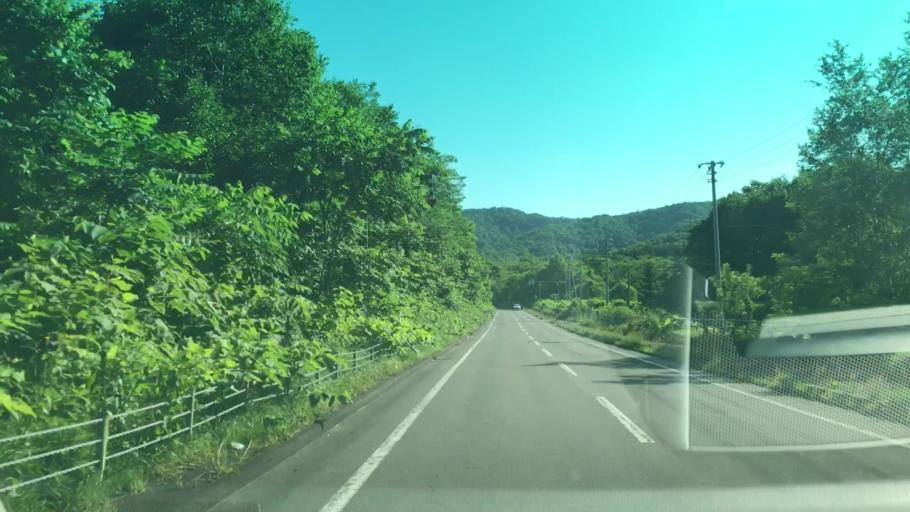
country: JP
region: Hokkaido
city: Yoichi
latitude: 43.0697
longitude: 140.7076
